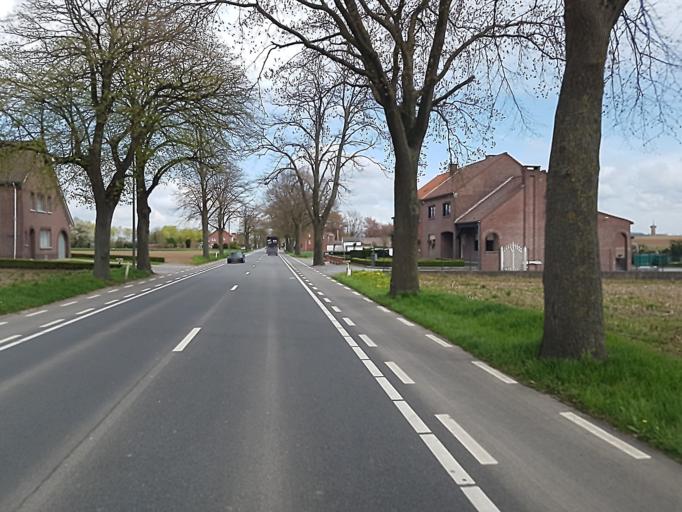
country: BE
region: Flanders
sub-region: Provincie Limburg
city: Riemst
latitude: 50.8168
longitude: 5.6078
